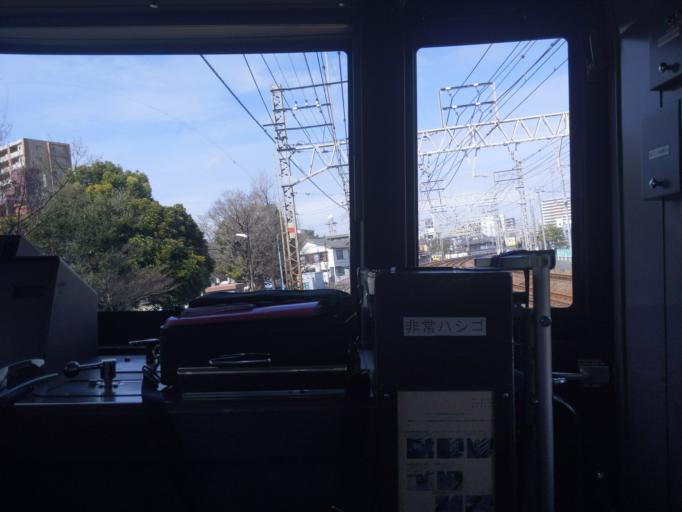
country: JP
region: Saitama
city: Soka
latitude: 35.7808
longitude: 139.7869
